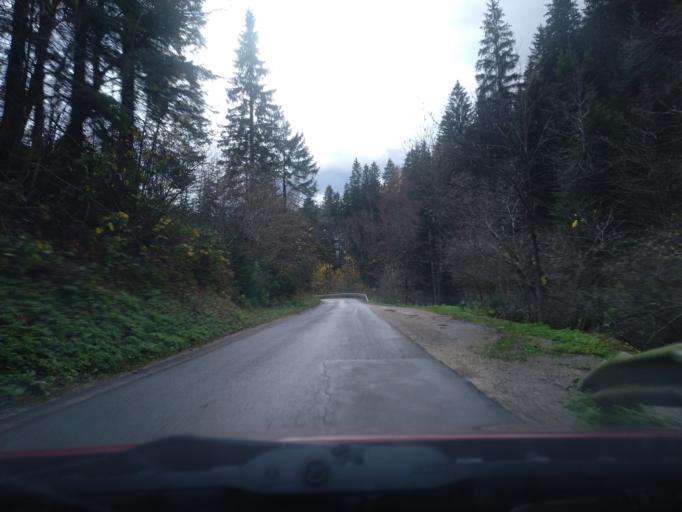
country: SI
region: Luce
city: Luce
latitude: 46.3078
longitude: 14.6994
